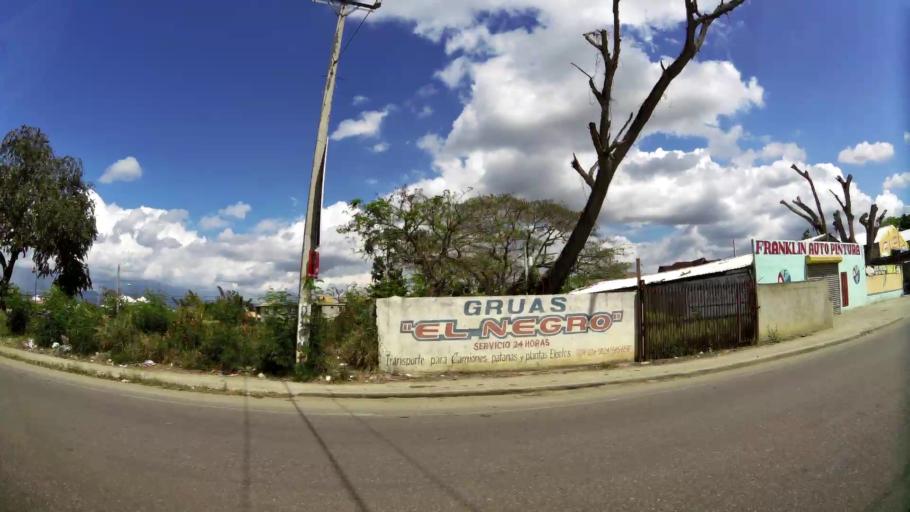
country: DO
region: Santiago
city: Santiago de los Caballeros
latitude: 19.4219
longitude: -70.6830
